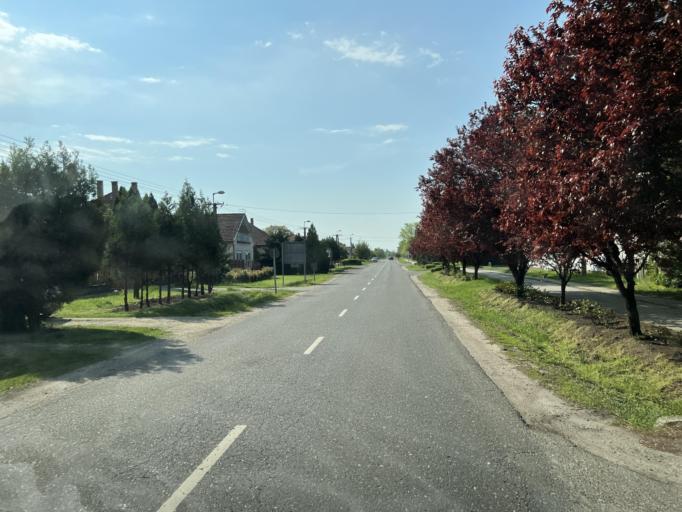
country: HU
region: Pest
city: Jaszkarajeno
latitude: 47.0974
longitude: 20.0233
